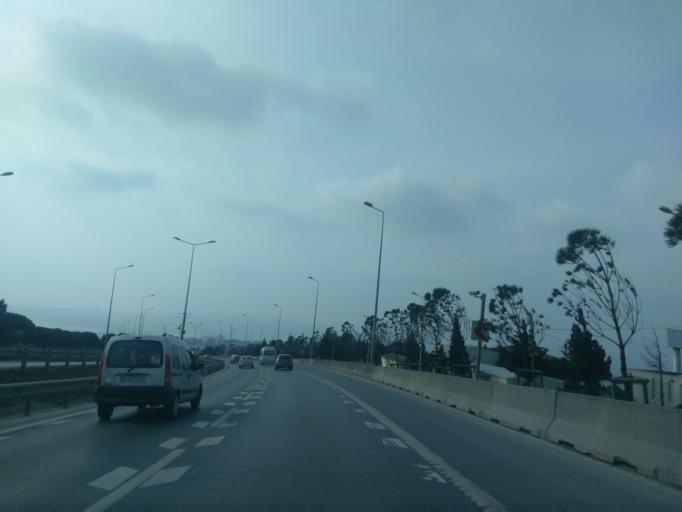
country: TR
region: Istanbul
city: Bueyuekcekmece
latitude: 41.0262
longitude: 28.6167
